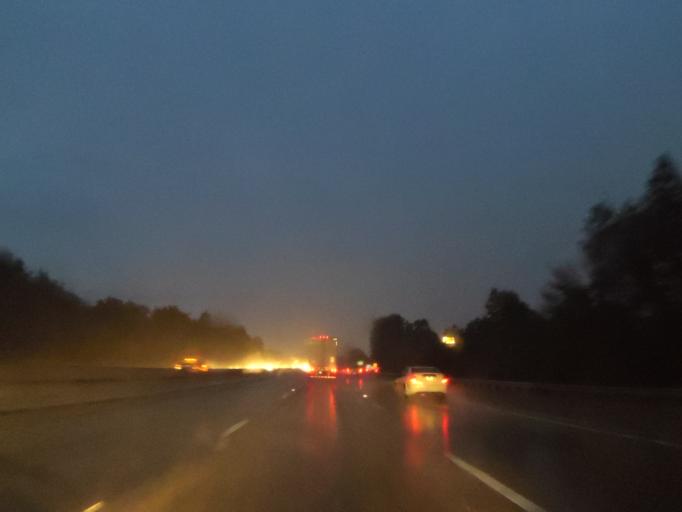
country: US
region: Tennessee
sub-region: Knox County
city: Farragut
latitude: 35.8974
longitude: -84.1798
